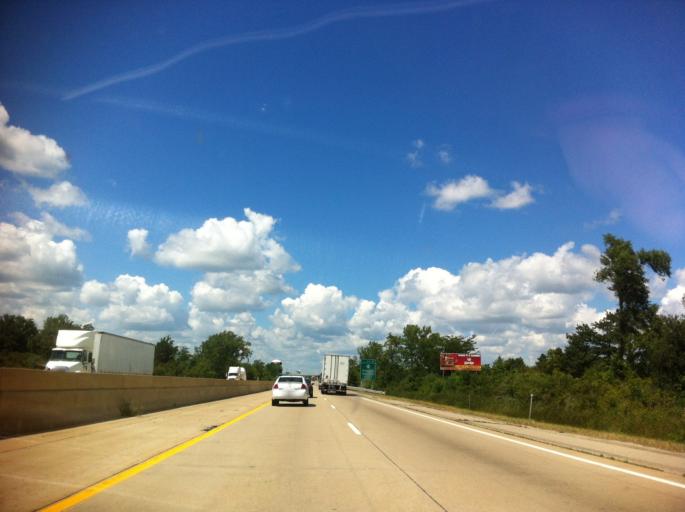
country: US
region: Michigan
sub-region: Monroe County
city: Dundee
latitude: 41.9441
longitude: -83.6650
